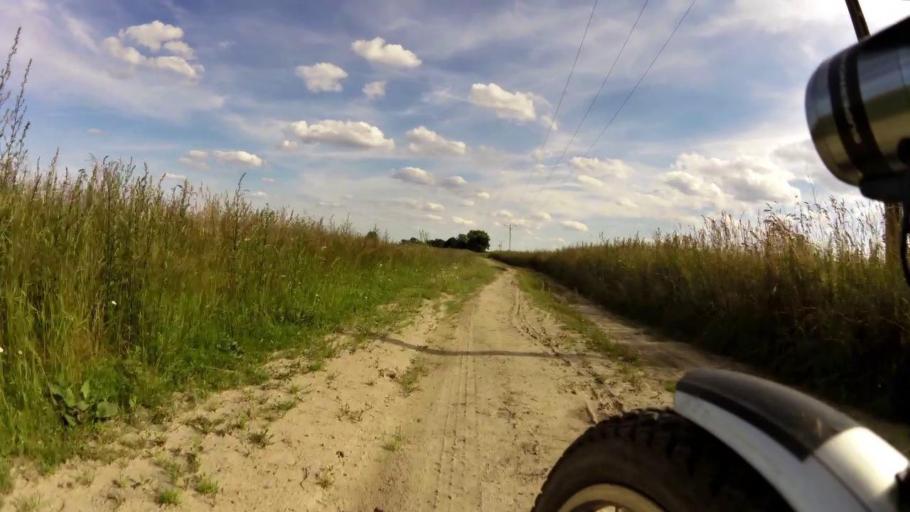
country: PL
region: West Pomeranian Voivodeship
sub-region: Powiat lobeski
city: Wegorzyno
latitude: 53.5635
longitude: 15.4723
